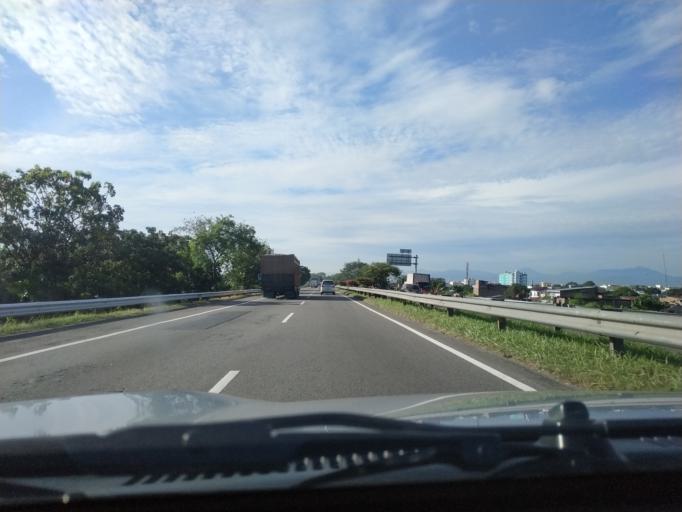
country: ID
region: North Sumatra
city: Medan
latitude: 3.5884
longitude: 98.7241
